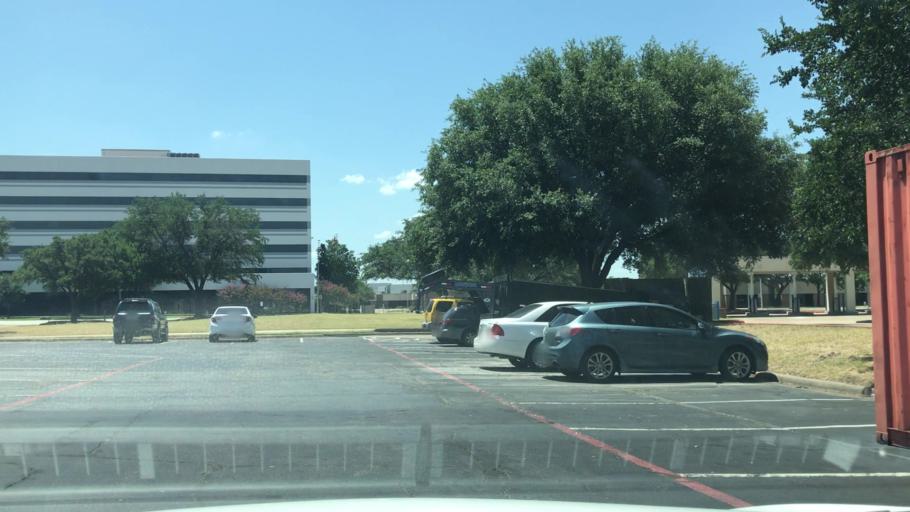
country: US
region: Texas
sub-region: Dallas County
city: Farmers Branch
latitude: 32.9233
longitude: -96.9020
